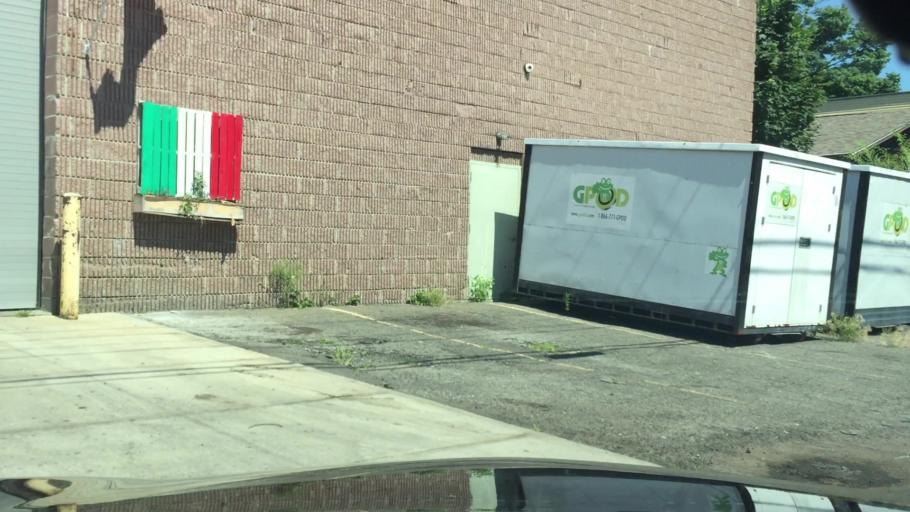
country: US
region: Connecticut
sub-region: Fairfield County
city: Stratford
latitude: 41.1815
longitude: -73.1566
